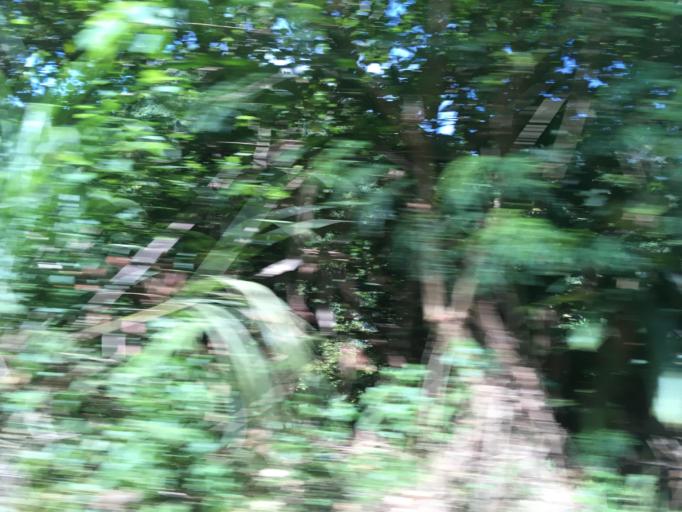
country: TW
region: Taiwan
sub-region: Yilan
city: Yilan
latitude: 24.4335
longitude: 121.7519
